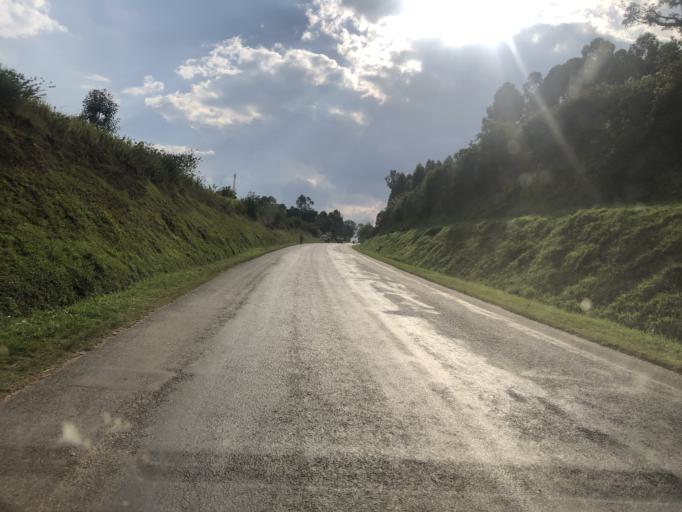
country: UG
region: Western Region
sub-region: Bushenyi District
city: Bushenyi
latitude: -0.5432
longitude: 30.2049
